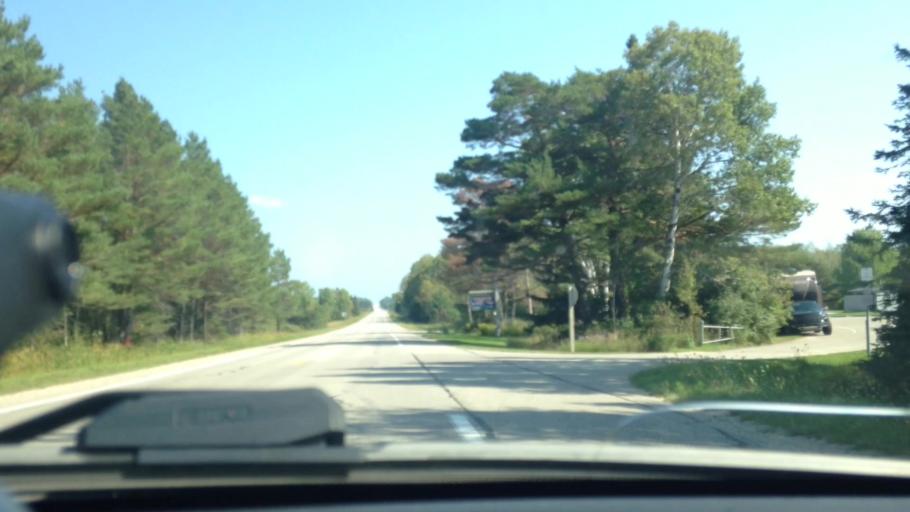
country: US
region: Michigan
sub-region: Luce County
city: Newberry
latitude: 46.3105
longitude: -85.5915
